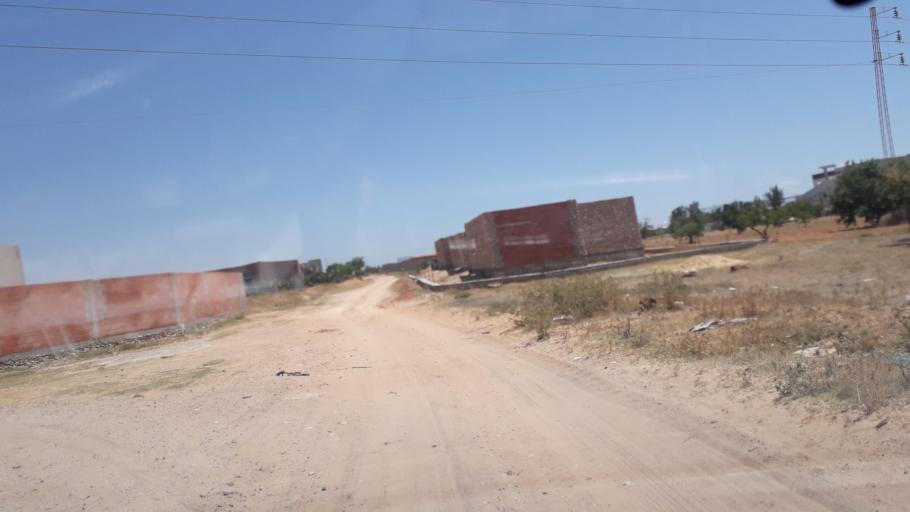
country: TN
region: Safaqis
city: Al Qarmadah
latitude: 34.8300
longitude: 10.7768
